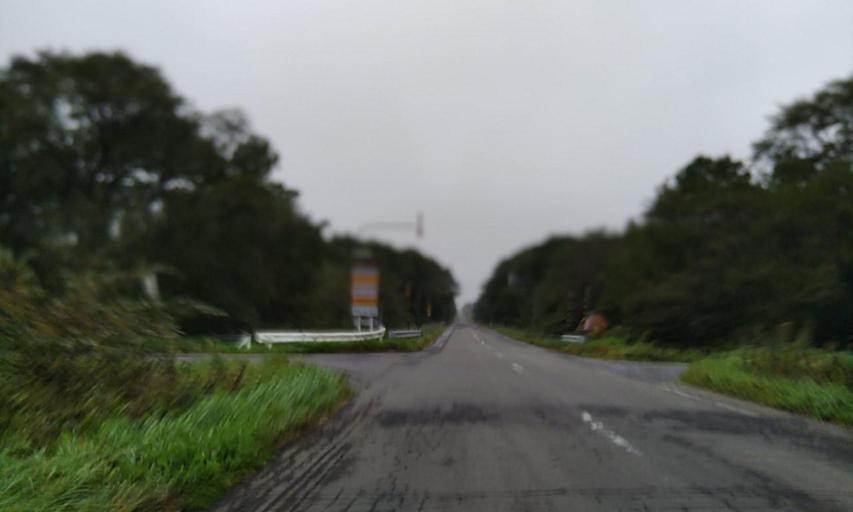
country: JP
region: Hokkaido
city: Shibetsu
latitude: 43.5200
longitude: 144.6843
